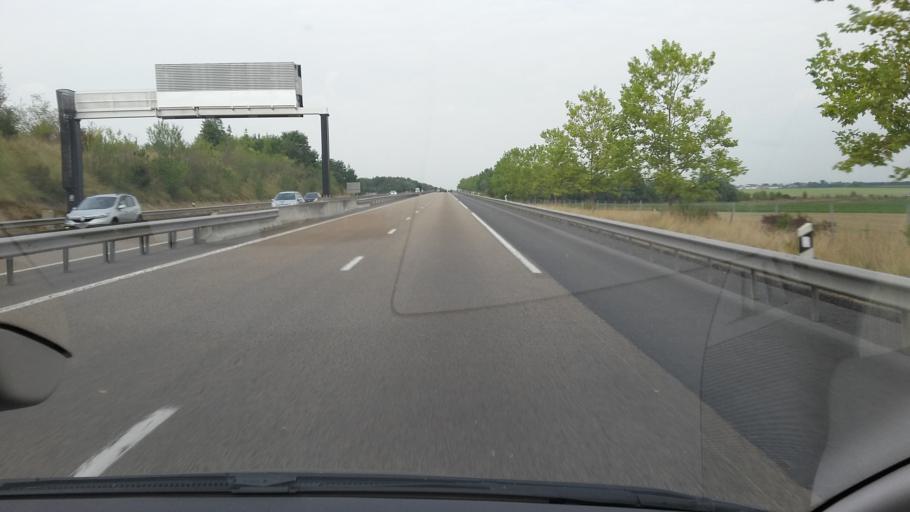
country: FR
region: Champagne-Ardenne
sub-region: Departement de la Marne
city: Witry-les-Reims
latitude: 49.2950
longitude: 4.1304
